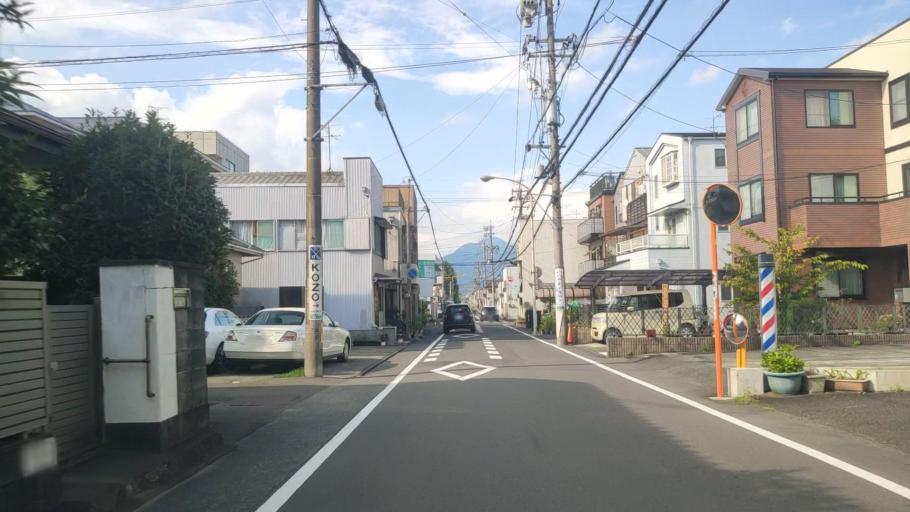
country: JP
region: Shizuoka
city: Shizuoka-shi
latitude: 34.9864
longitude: 138.3859
